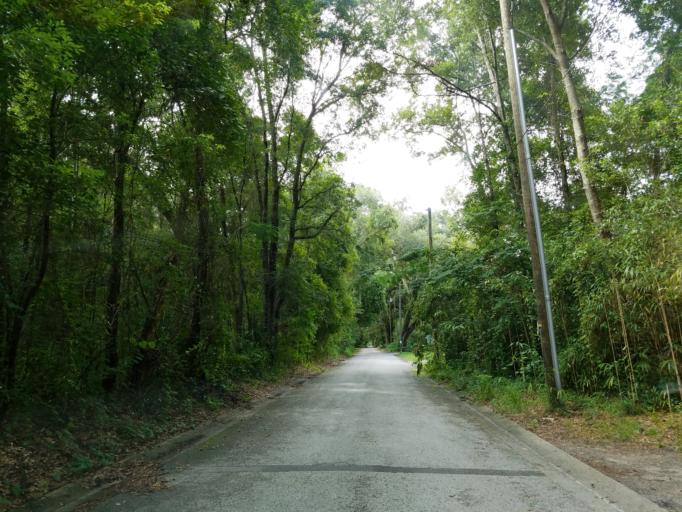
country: US
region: Florida
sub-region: Alachua County
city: Gainesville
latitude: 29.5008
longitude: -82.2875
